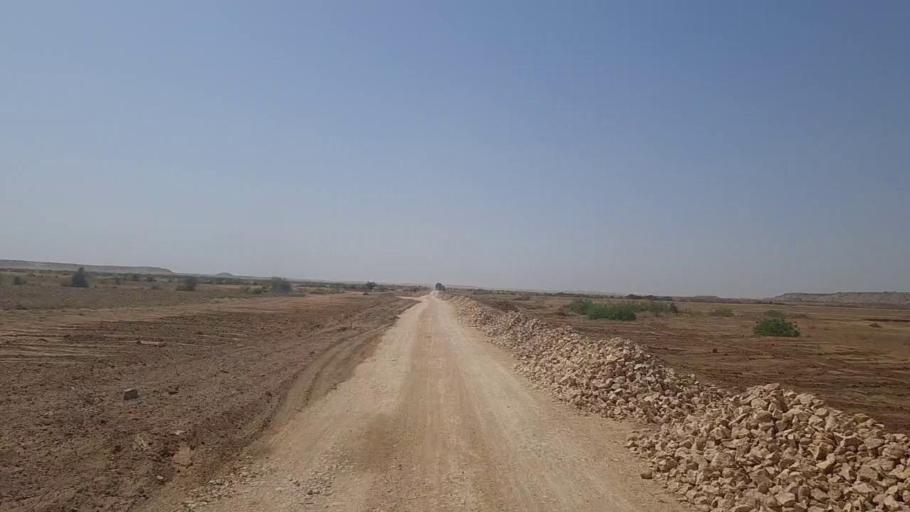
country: PK
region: Sindh
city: Kotri
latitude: 25.1468
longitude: 68.1868
